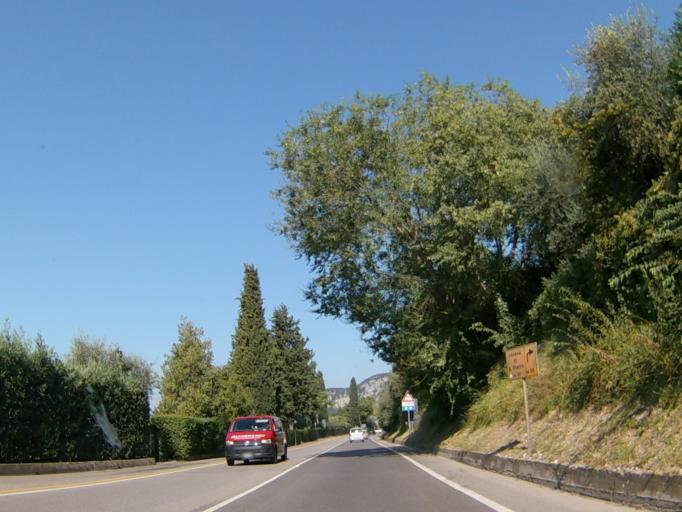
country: IT
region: Veneto
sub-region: Provincia di Verona
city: Garda
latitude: 45.5651
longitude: 10.7123
